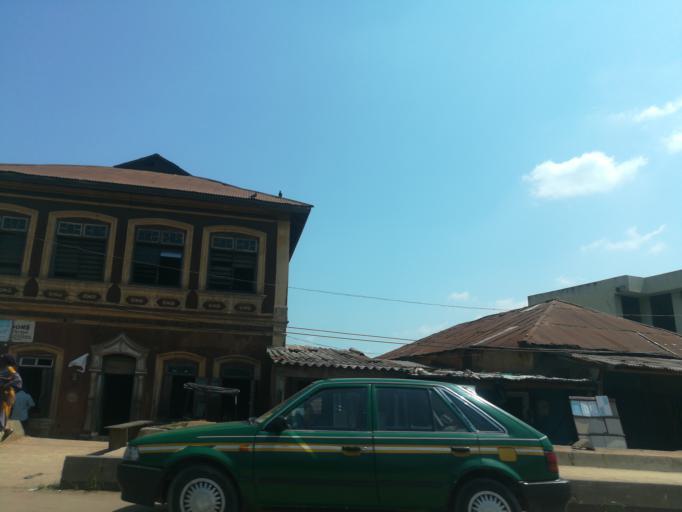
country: NG
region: Ogun
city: Abeokuta
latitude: 7.1643
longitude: 3.3565
